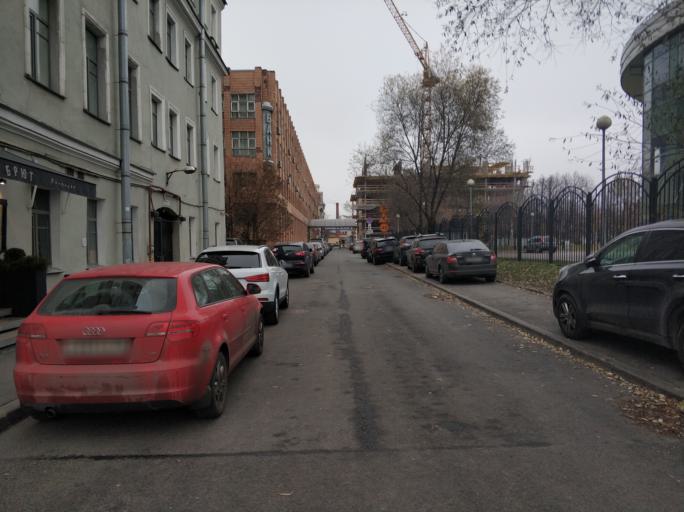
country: RU
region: Leningrad
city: Sampsonievskiy
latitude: 59.9694
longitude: 30.3371
